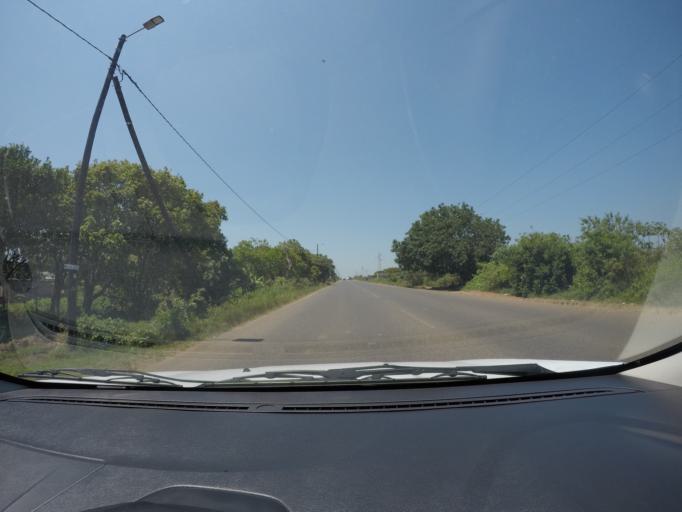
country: ZA
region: KwaZulu-Natal
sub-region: uThungulu District Municipality
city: eSikhawini
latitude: -28.8432
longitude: 31.9337
